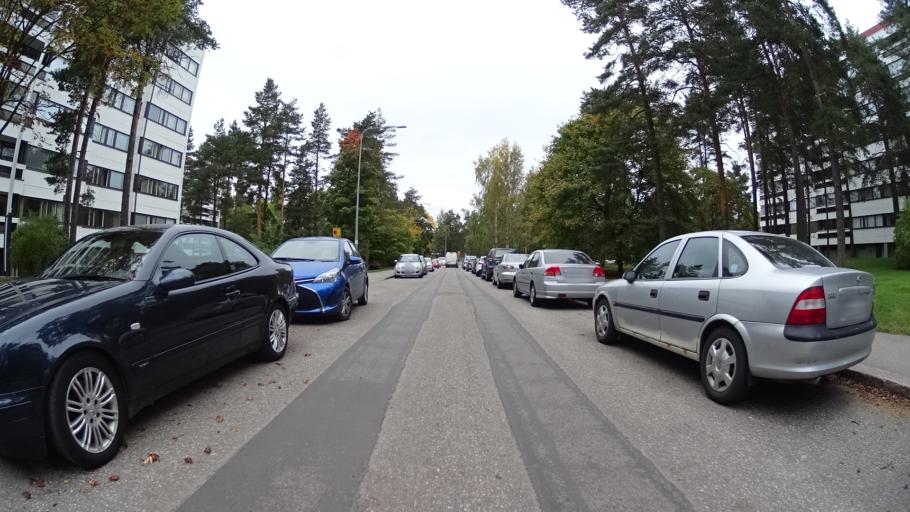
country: FI
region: Uusimaa
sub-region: Helsinki
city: Vantaa
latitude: 60.2266
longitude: 25.0705
